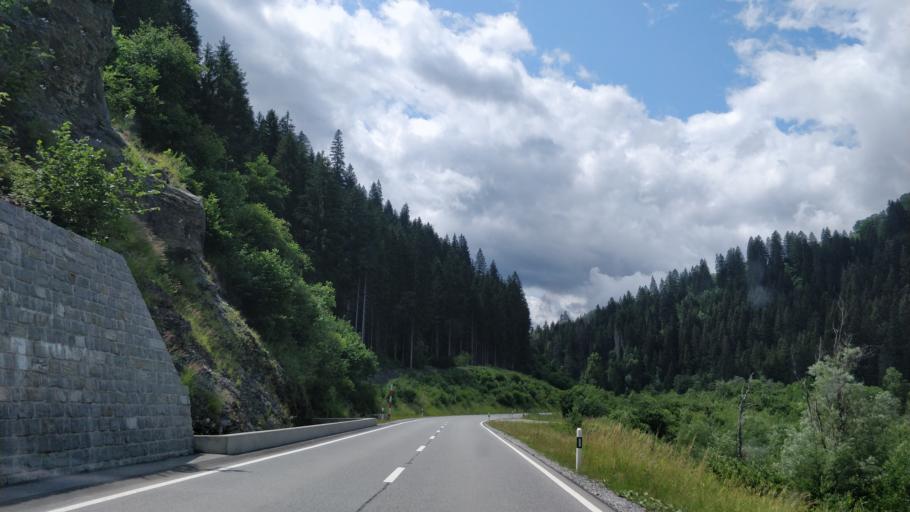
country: CH
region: Grisons
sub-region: Surselva District
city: Ilanz
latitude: 46.7266
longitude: 9.2078
